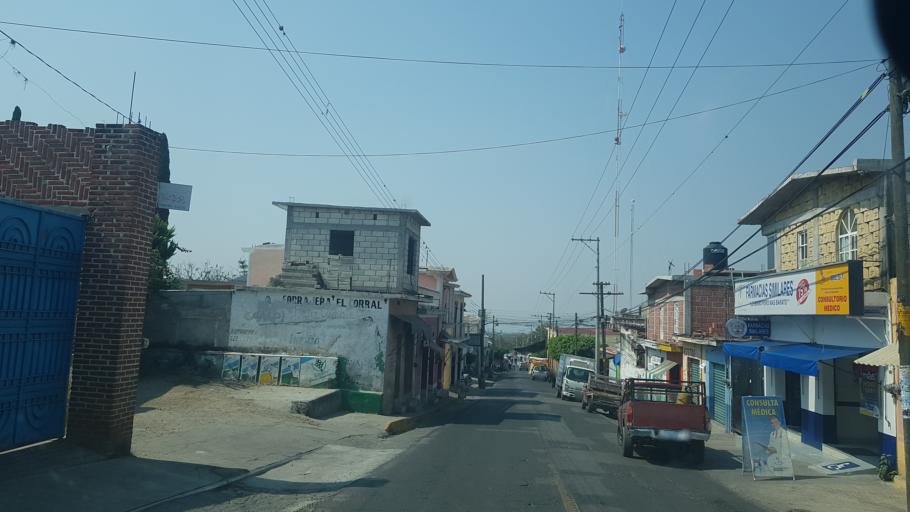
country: MX
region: Morelos
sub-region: Temoac
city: Temoac
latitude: 18.7733
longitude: -98.7775
